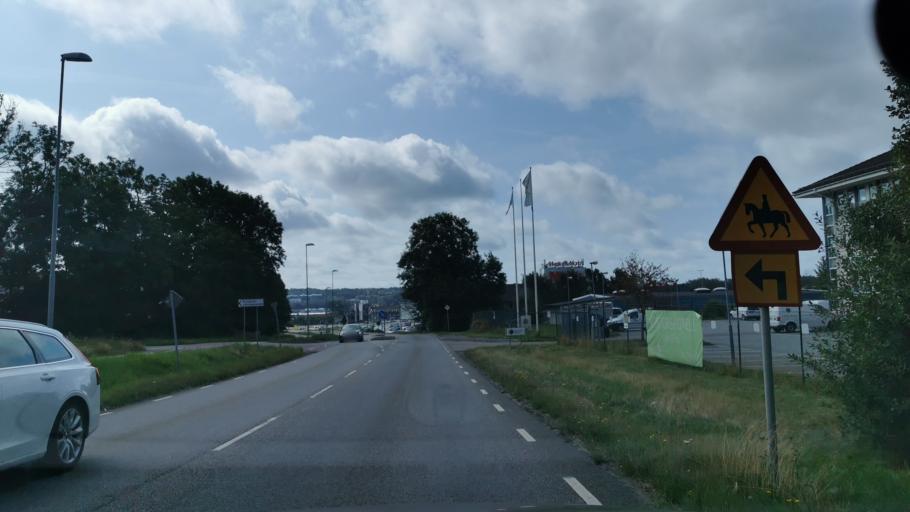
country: SE
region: Vaestra Goetaland
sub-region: Goteborg
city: Majorna
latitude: 57.6539
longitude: 11.9510
